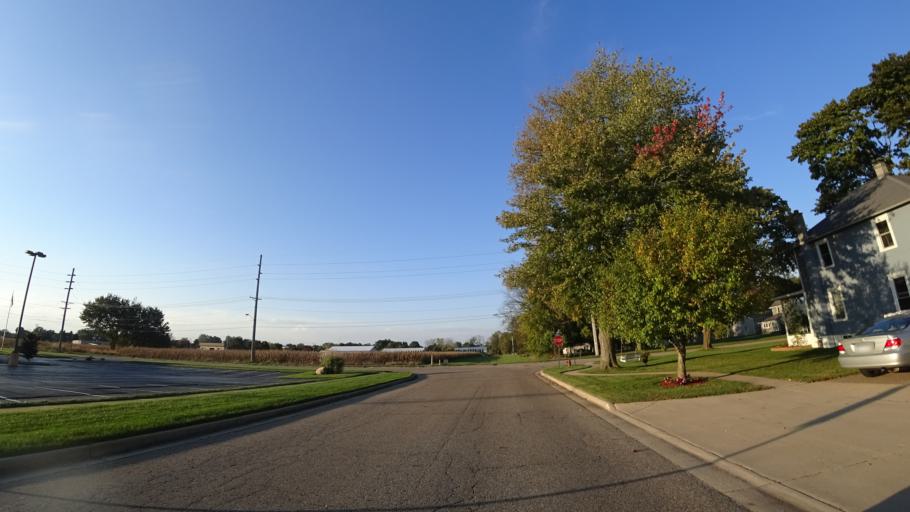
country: US
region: Michigan
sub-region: Saint Joseph County
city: Three Rivers
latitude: 41.9488
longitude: -85.6444
